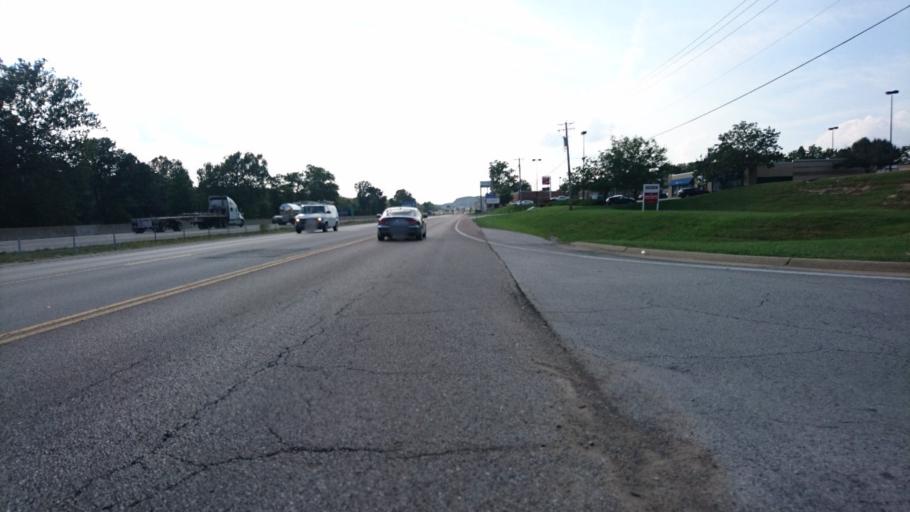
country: US
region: Missouri
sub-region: Saint Louis County
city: Eureka
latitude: 38.5046
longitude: -90.6567
